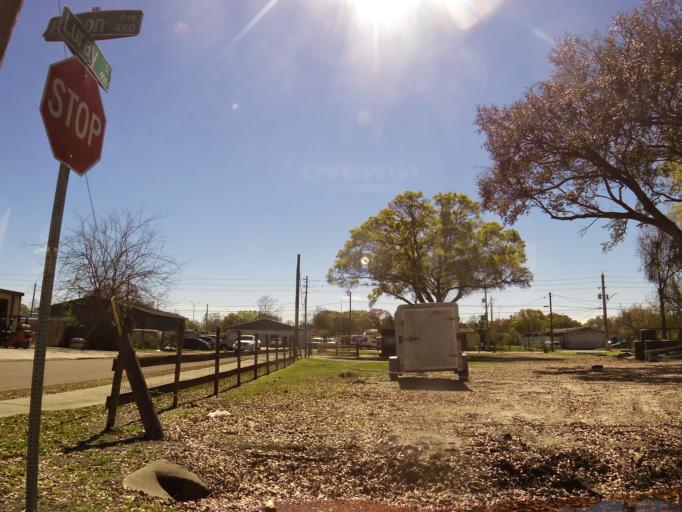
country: US
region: Florida
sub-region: Duval County
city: Jacksonville
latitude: 30.3225
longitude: -81.7192
